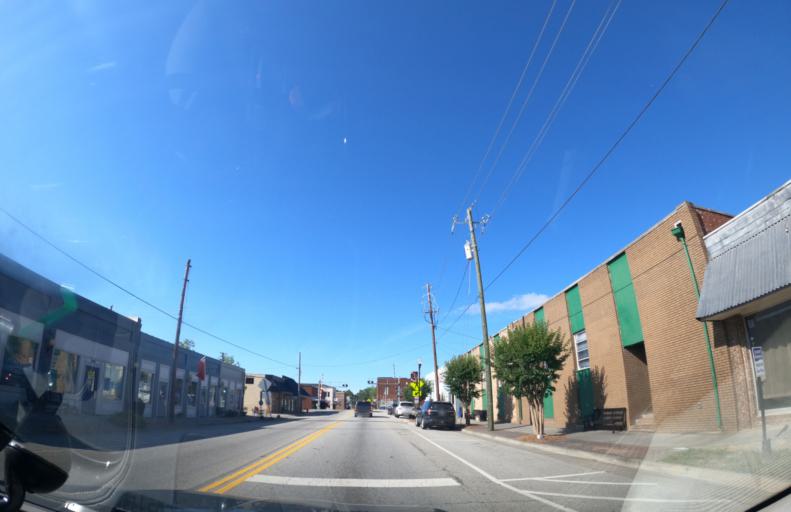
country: US
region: Georgia
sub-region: Columbia County
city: Harlem
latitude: 33.4166
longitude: -82.3121
